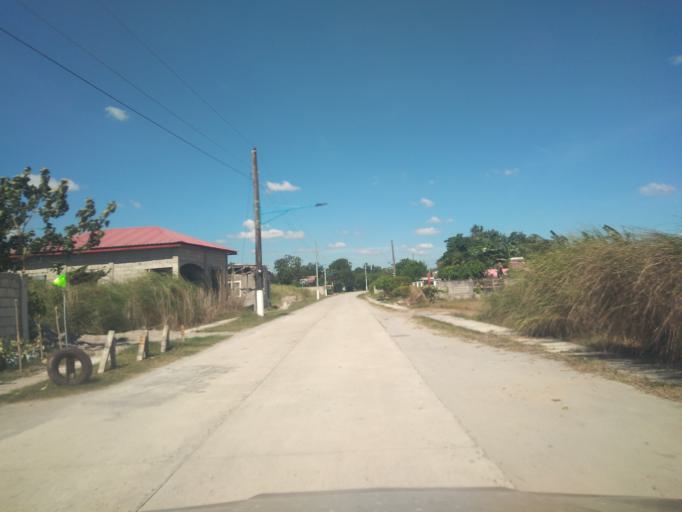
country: PH
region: Central Luzon
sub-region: Province of Pampanga
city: Balas
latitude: 15.0415
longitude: 120.6156
